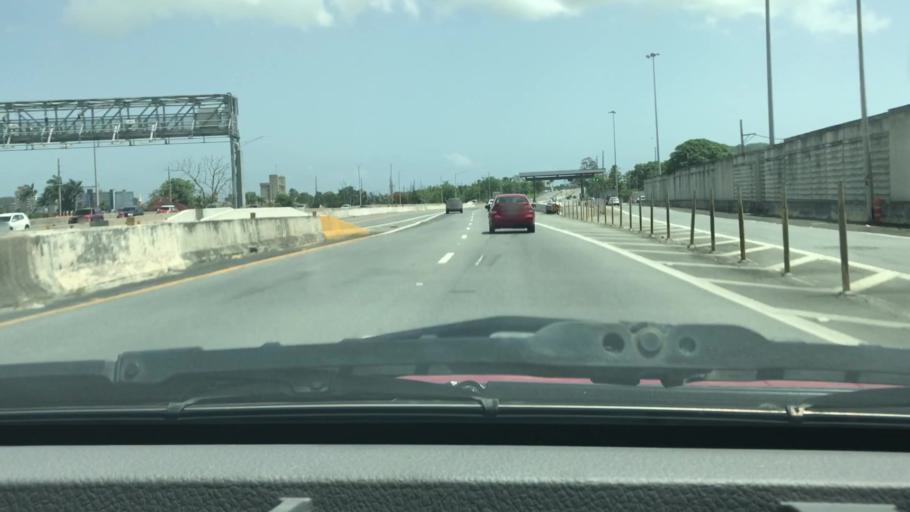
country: PR
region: Bayamon
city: Bayamon
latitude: 18.3863
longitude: -66.1550
